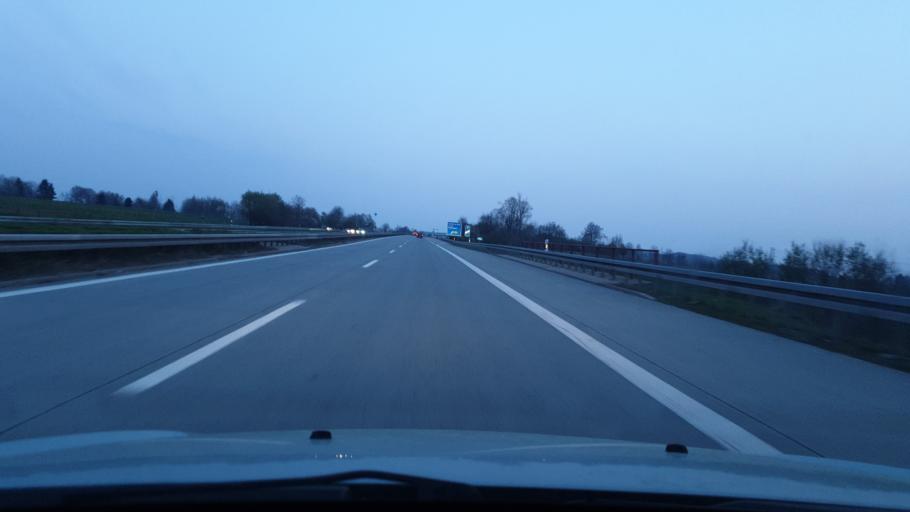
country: DE
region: Saxony
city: Niederdorf
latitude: 50.7329
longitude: 12.7798
